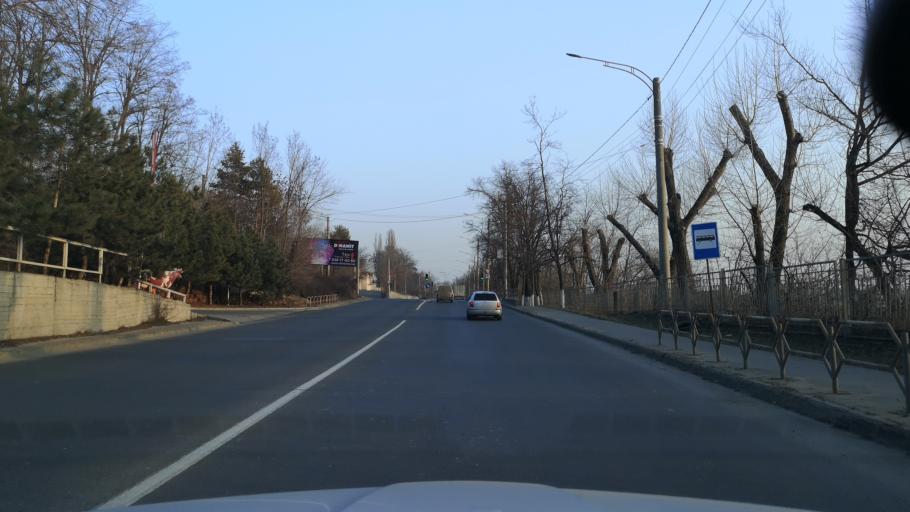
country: MD
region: Chisinau
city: Chisinau
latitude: 47.0507
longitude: 28.8205
